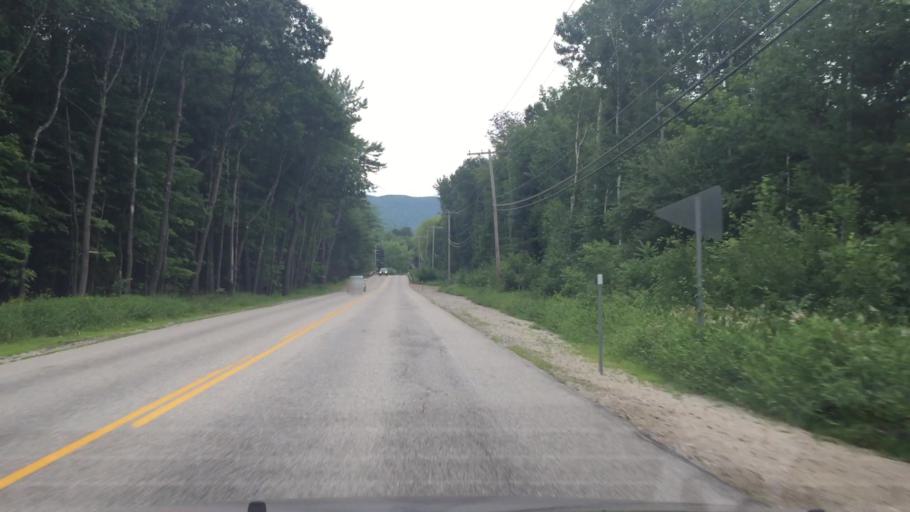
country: US
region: New Hampshire
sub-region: Carroll County
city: North Conway
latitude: 44.0568
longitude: -71.1437
